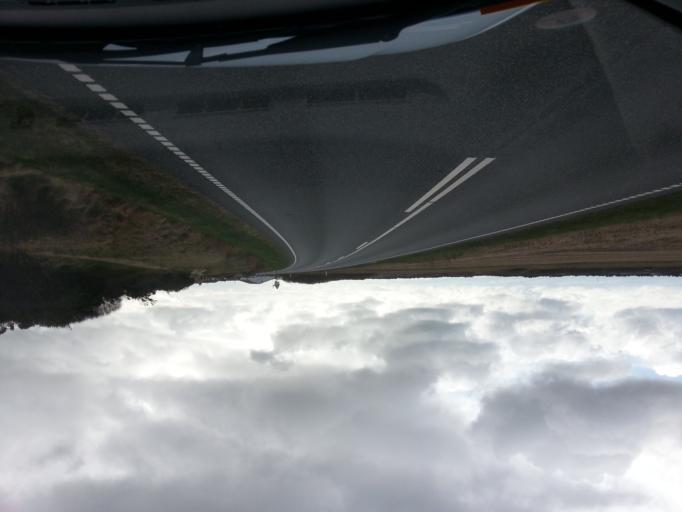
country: DK
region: Central Jutland
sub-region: Ringkobing-Skjern Kommune
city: Ringkobing
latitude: 56.1482
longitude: 8.1259
